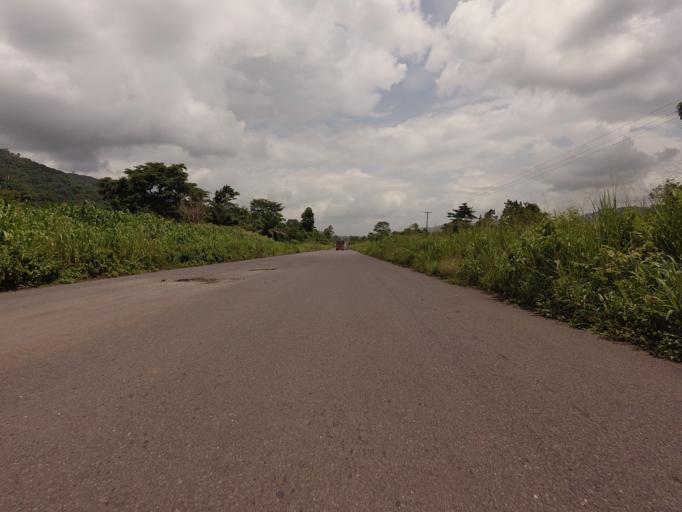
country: GH
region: Volta
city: Ho
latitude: 6.5719
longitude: 0.2739
